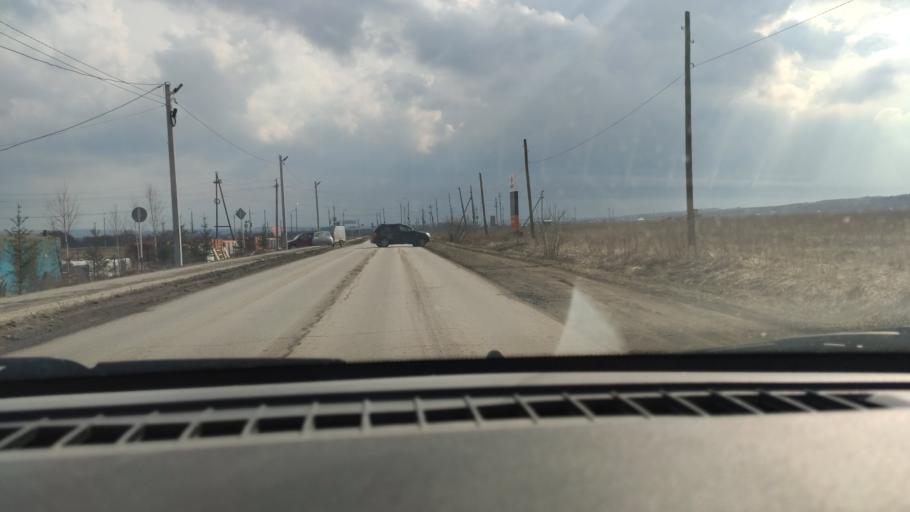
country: RU
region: Perm
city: Kultayevo
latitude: 57.8869
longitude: 55.9234
